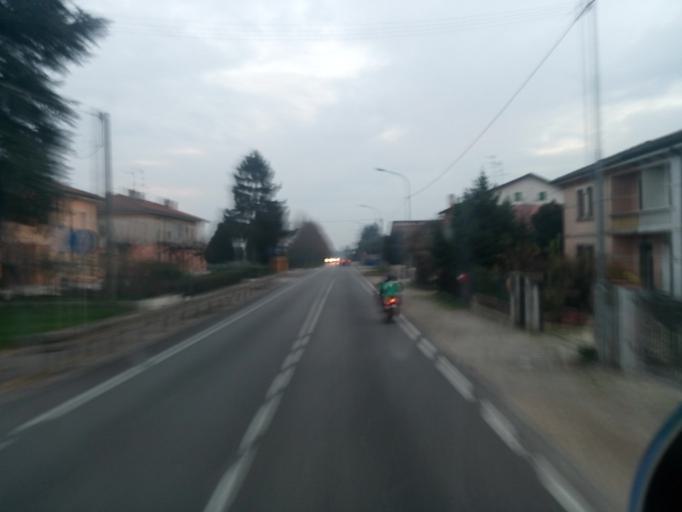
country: IT
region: Lombardy
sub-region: Provincia di Mantova
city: Roncoferraro
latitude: 45.1453
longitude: 10.9273
